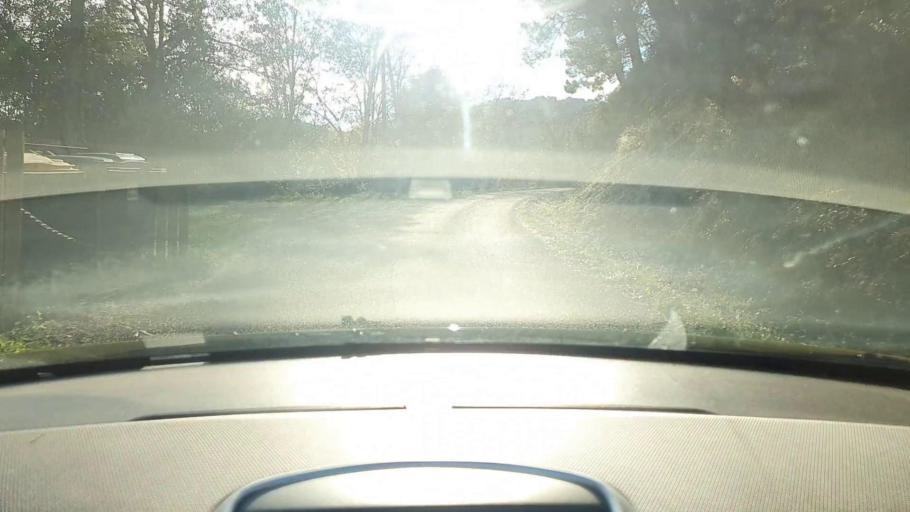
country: FR
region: Languedoc-Roussillon
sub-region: Departement du Gard
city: Branoux-les-Taillades
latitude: 44.2376
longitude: 3.9840
